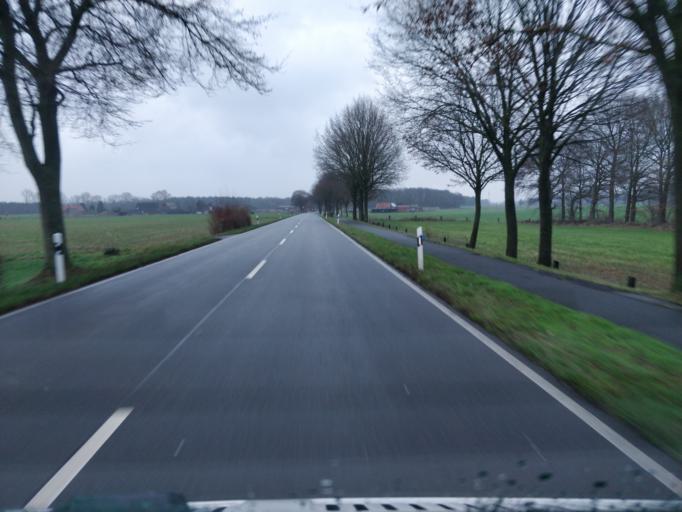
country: DE
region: North Rhine-Westphalia
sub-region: Regierungsbezirk Dusseldorf
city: Mehrhoog
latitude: 51.7590
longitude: 6.5177
